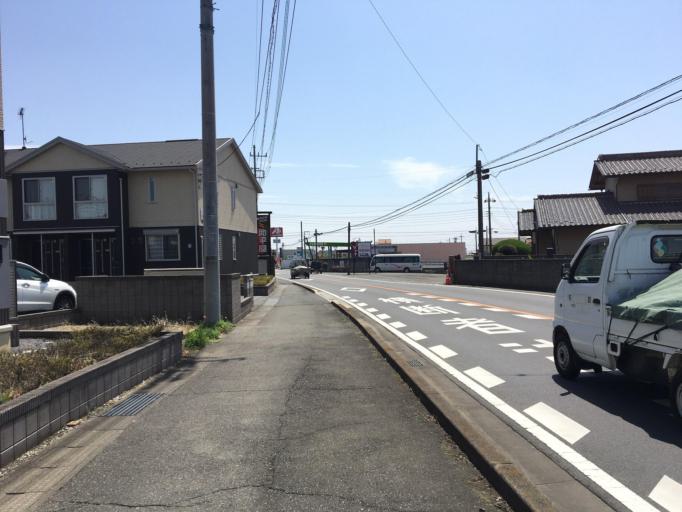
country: JP
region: Gunma
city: Sakai-nakajima
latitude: 36.2784
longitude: 139.3059
